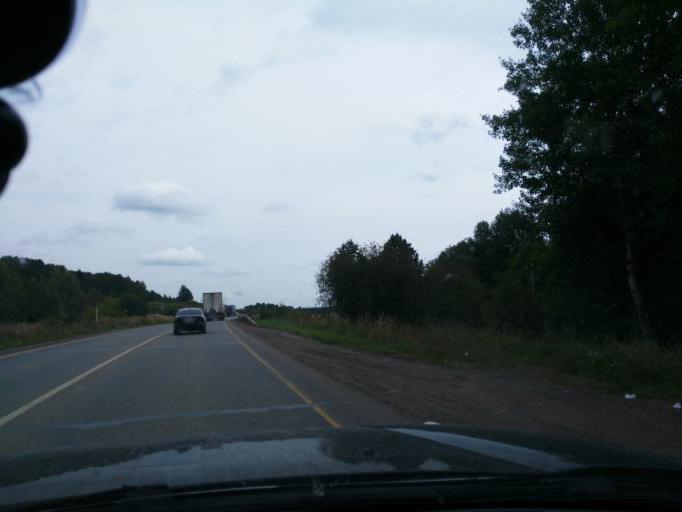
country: RU
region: Perm
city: Kuyeda
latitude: 56.4599
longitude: 55.6335
